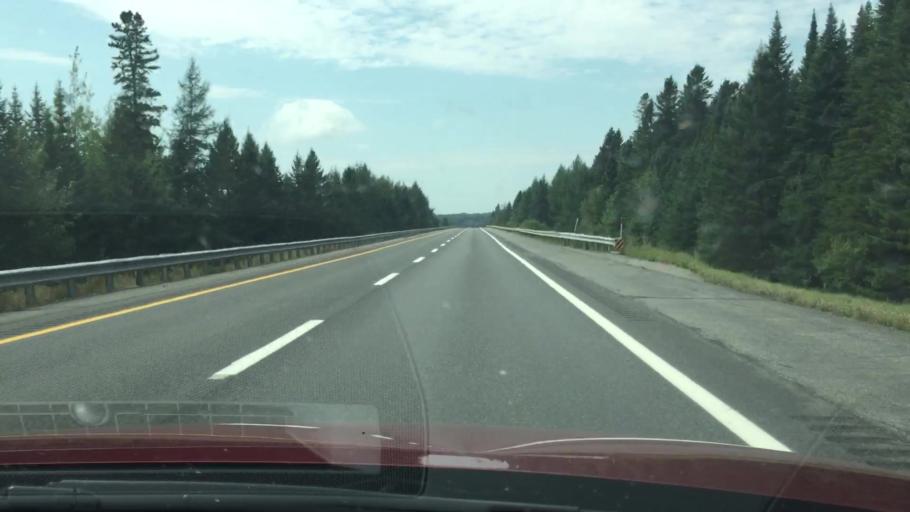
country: US
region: Maine
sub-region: Aroostook County
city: Hodgdon
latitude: 46.1144
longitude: -68.1439
